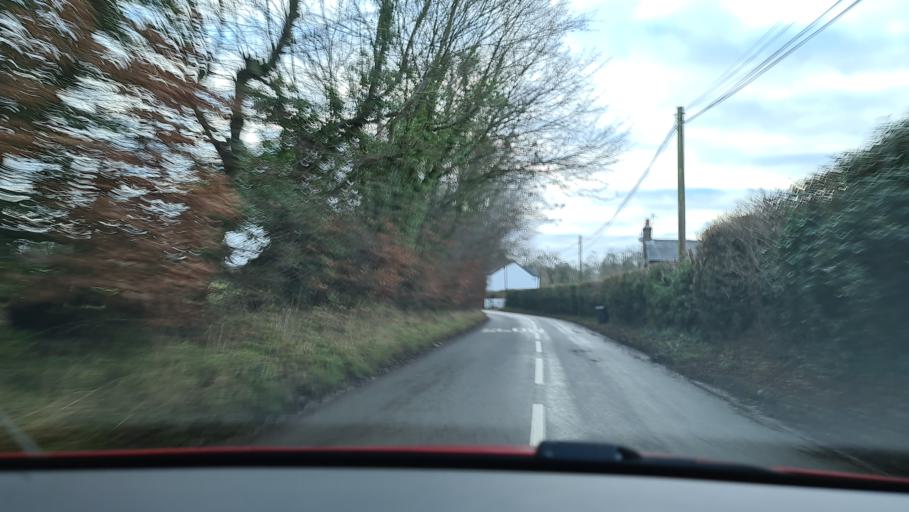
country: GB
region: England
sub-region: Buckinghamshire
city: Great Missenden
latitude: 51.7400
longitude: -0.7027
